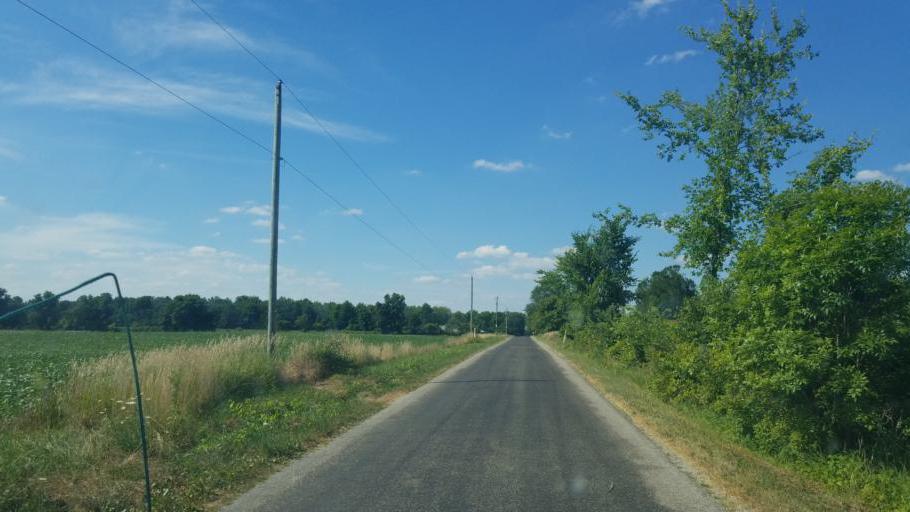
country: US
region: Ohio
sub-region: Defiance County
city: Hicksville
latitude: 41.3730
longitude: -84.7863
